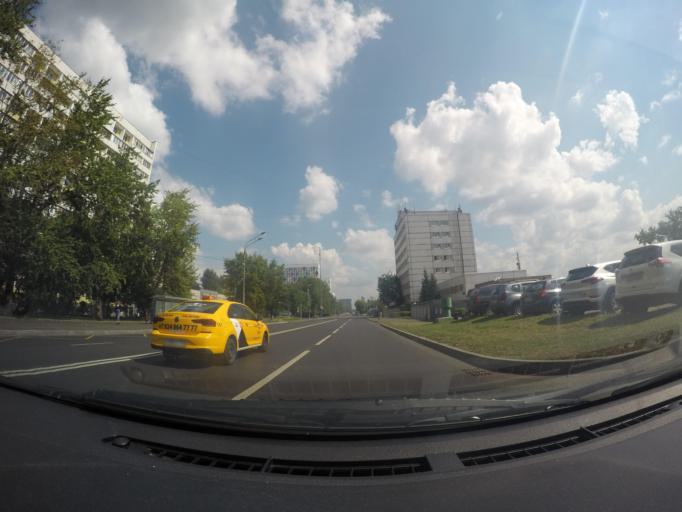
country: RU
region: Moscow
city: Kozeyevo
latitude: 55.8522
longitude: 37.6109
